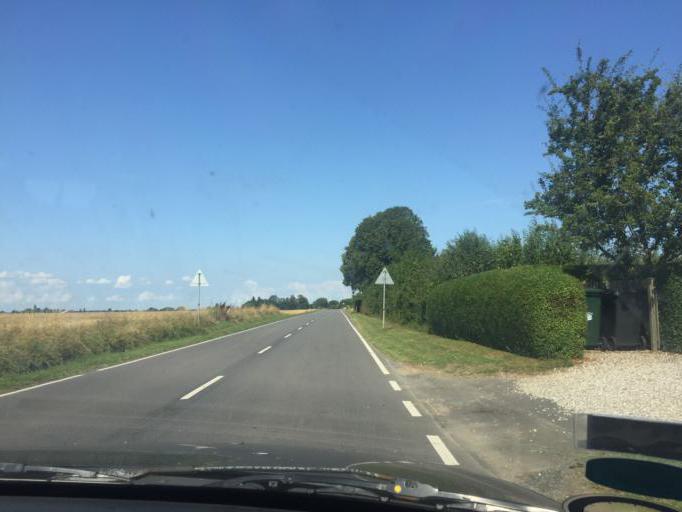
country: DK
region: Zealand
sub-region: Guldborgsund Kommune
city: Sakskobing
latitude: 54.7933
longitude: 11.5704
